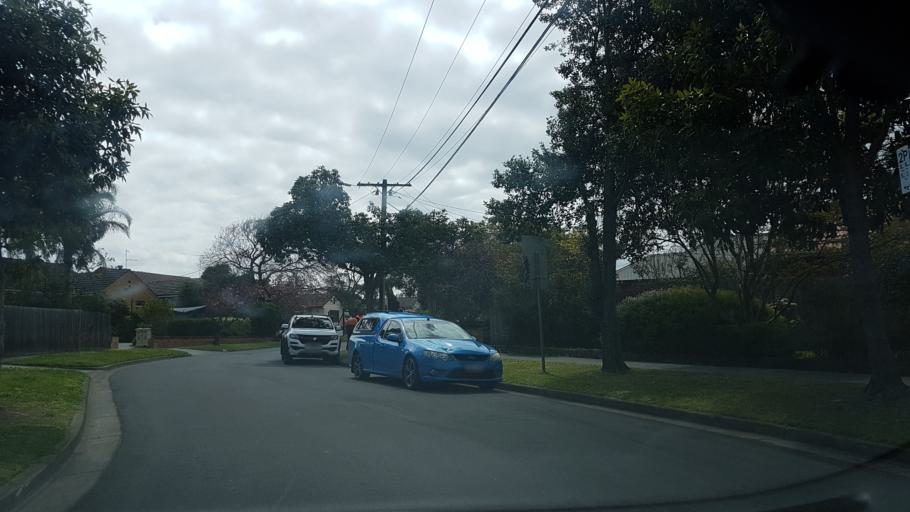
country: AU
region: Victoria
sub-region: Bayside
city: Moorabbin
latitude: -37.9289
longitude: 145.0348
